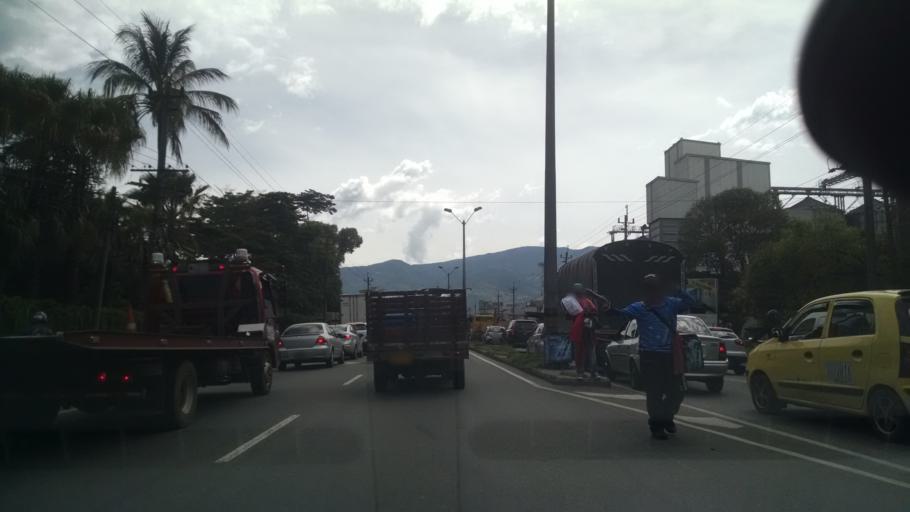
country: CO
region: Antioquia
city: Envigado
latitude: 6.1695
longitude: -75.6047
